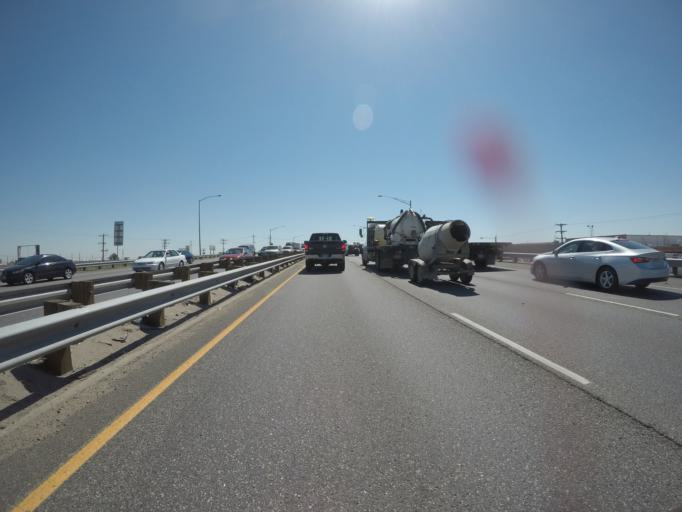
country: US
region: Colorado
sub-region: Adams County
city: Commerce City
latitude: 39.7801
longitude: -104.9339
